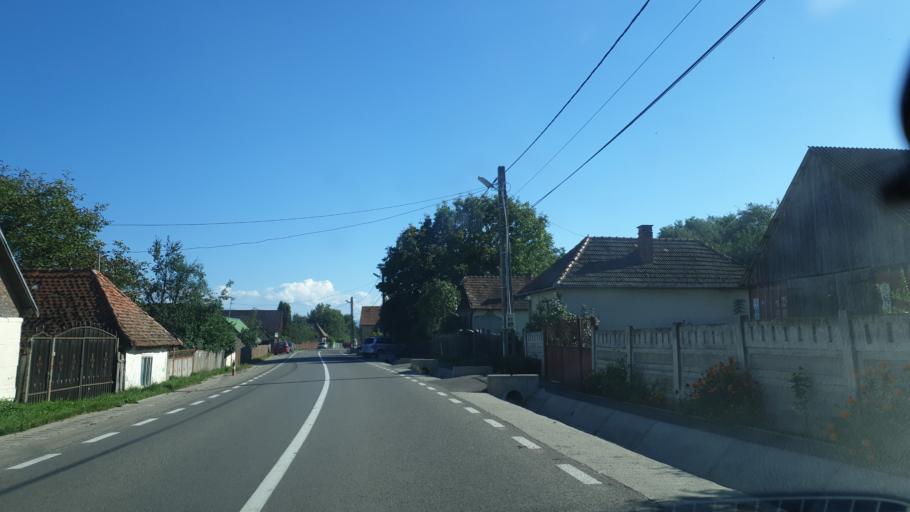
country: RO
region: Covasna
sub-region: Comuna Ilieni
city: Ilieni
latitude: 45.8023
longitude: 25.7694
